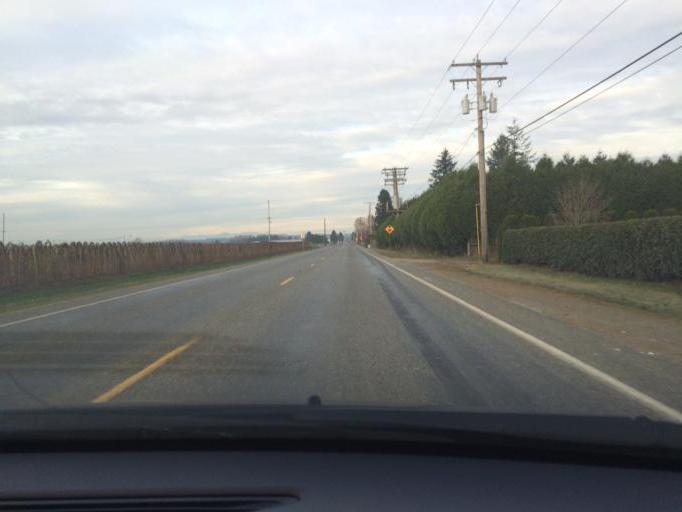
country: US
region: Washington
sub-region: Whatcom County
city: Ferndale
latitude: 48.9332
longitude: -122.5745
